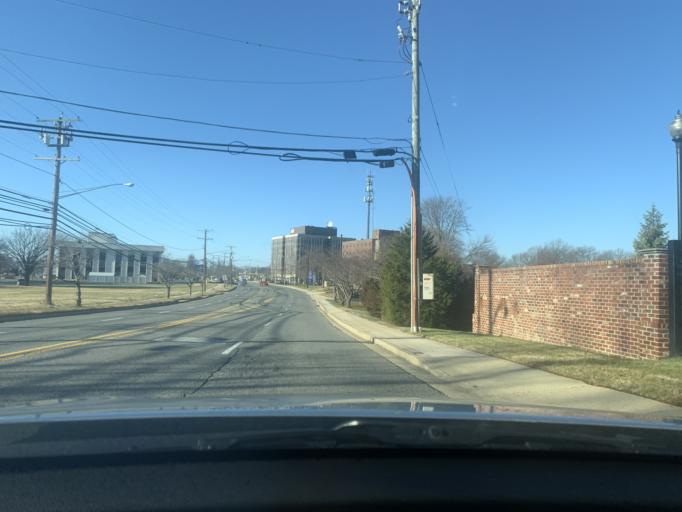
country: US
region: Maryland
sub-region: Prince George's County
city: Camp Springs
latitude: 38.8235
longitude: -76.9141
